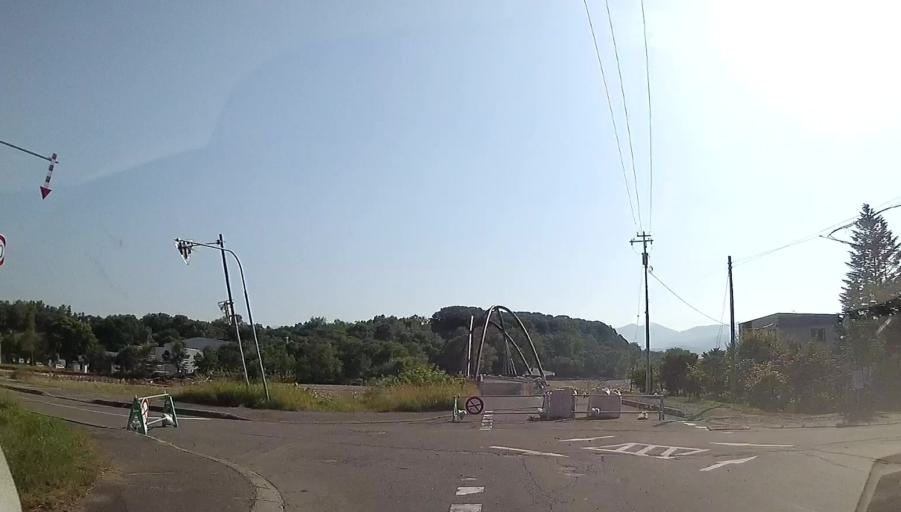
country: JP
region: Hokkaido
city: Otofuke
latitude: 43.0078
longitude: 142.8737
